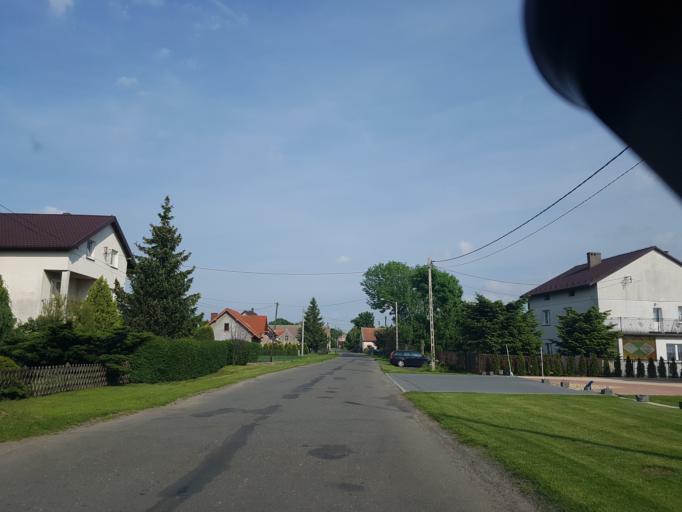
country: PL
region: Lower Silesian Voivodeship
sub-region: Powiat olawski
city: Wierzbno
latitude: 50.9102
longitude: 17.1170
